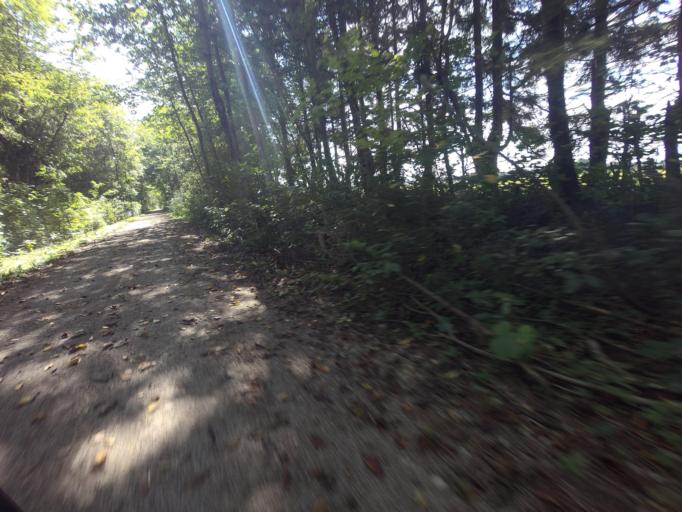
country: CA
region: Ontario
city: Huron East
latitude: 43.6944
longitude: -81.3340
